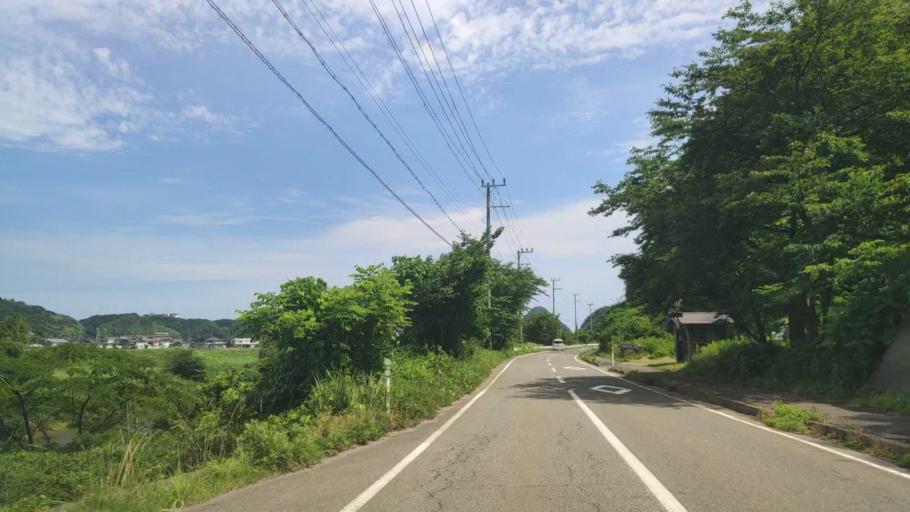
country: JP
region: Hyogo
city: Toyooka
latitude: 35.6435
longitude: 134.7622
